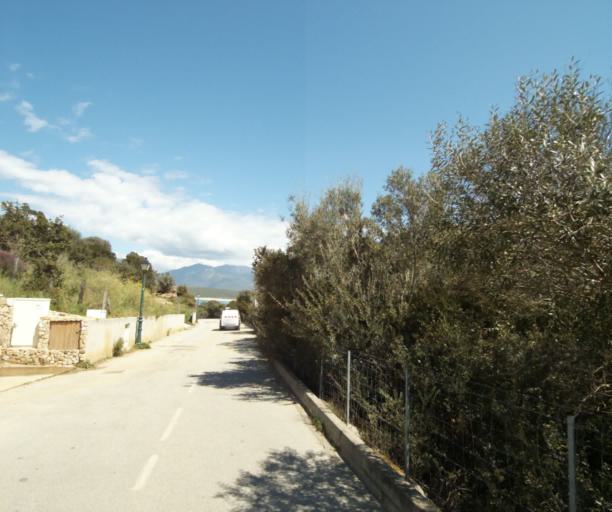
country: FR
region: Corsica
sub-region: Departement de la Corse-du-Sud
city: Propriano
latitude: 41.6425
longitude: 8.8679
